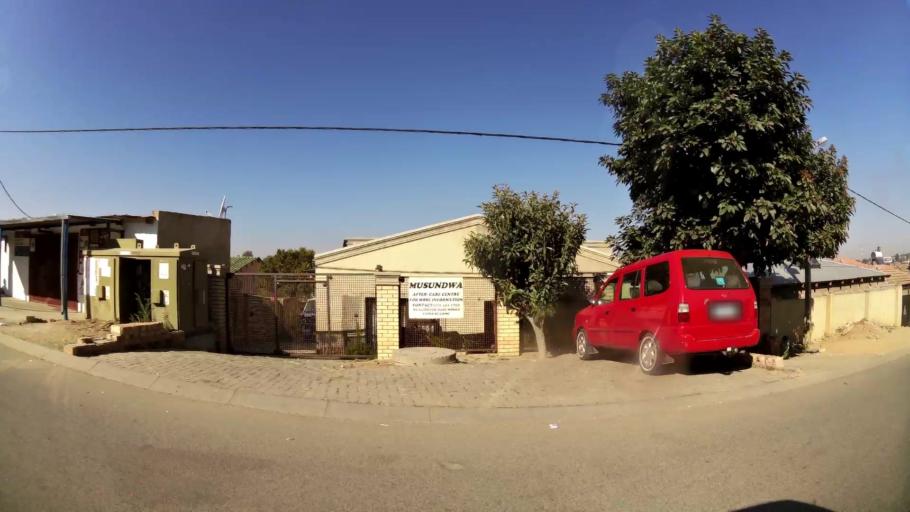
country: ZA
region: Gauteng
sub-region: City of Johannesburg Metropolitan Municipality
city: Modderfontein
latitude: -26.1092
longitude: 28.1179
